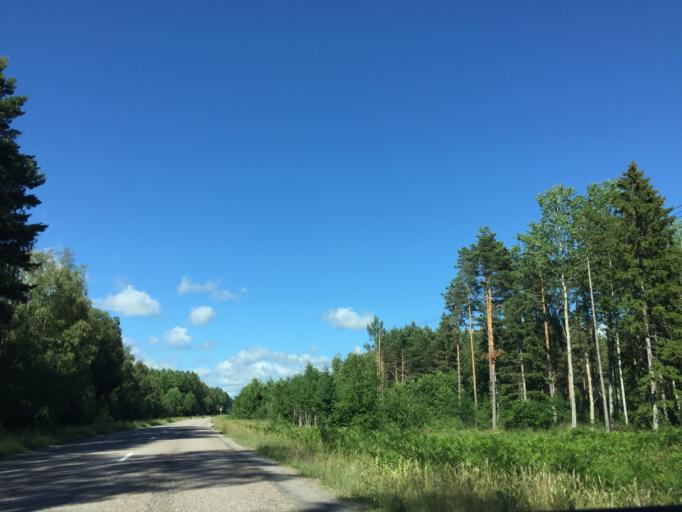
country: LV
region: Ventspils
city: Ventspils
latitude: 57.4841
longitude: 21.6730
